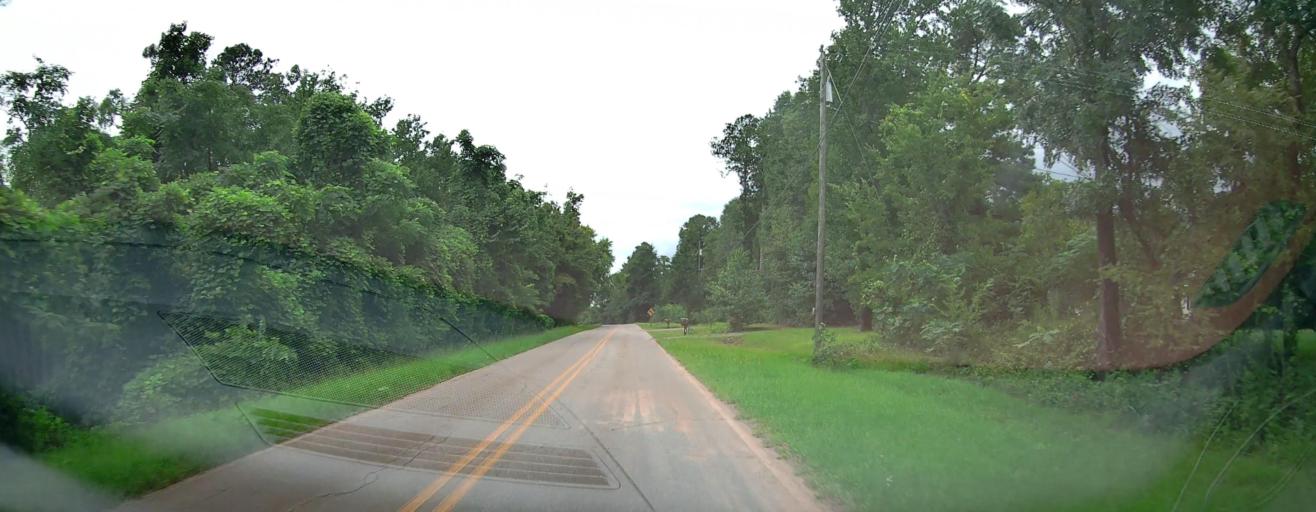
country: US
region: Georgia
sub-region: Bibb County
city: Macon
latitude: 32.7792
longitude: -83.5130
